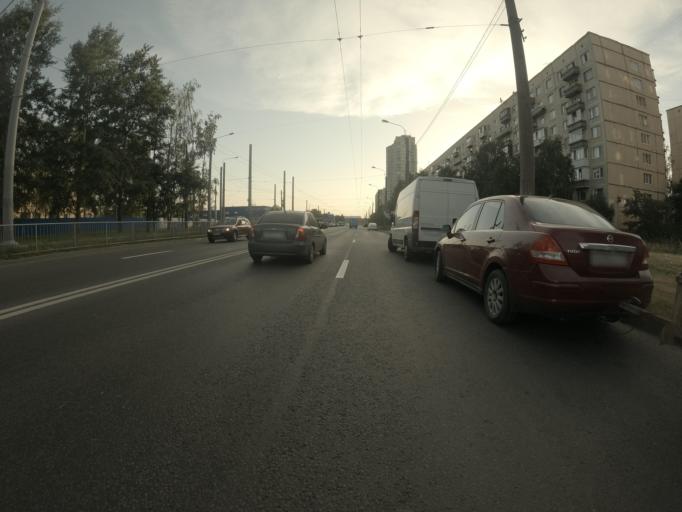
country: RU
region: St.-Petersburg
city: Krasnogvargeisky
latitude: 59.9366
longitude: 30.4824
